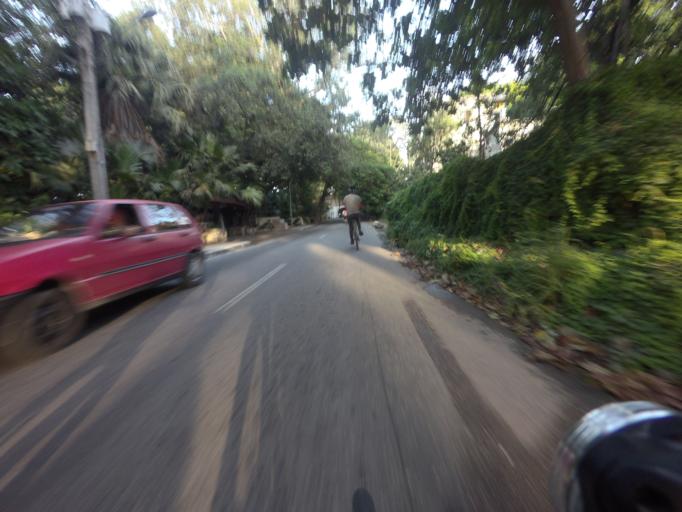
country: CU
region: La Habana
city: Havana
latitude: 23.1179
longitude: -82.4098
